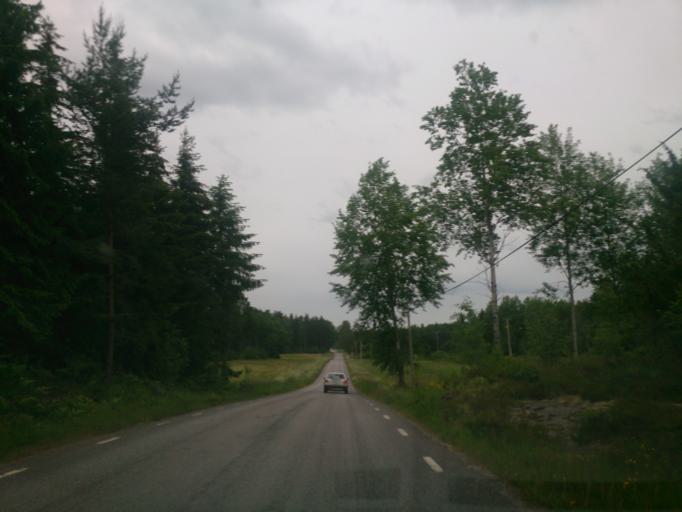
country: SE
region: OEstergoetland
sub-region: Valdemarsviks Kommun
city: Gusum
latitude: 58.3194
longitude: 16.3790
